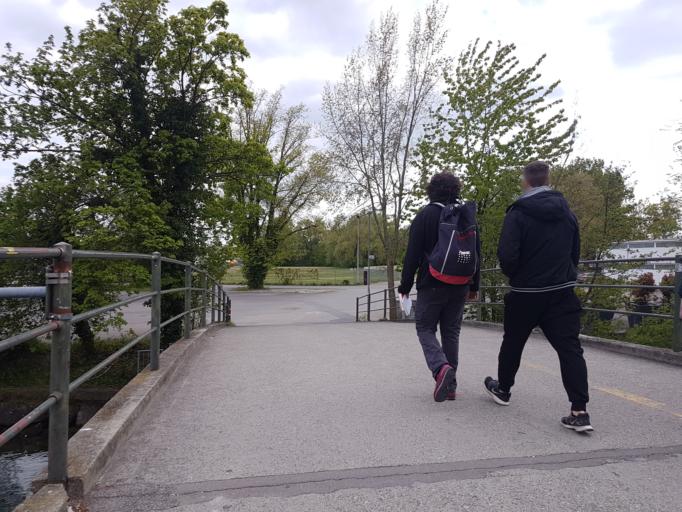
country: CH
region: Bern
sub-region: Biel/Bienne District
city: Nidau
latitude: 47.1303
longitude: 7.2364
